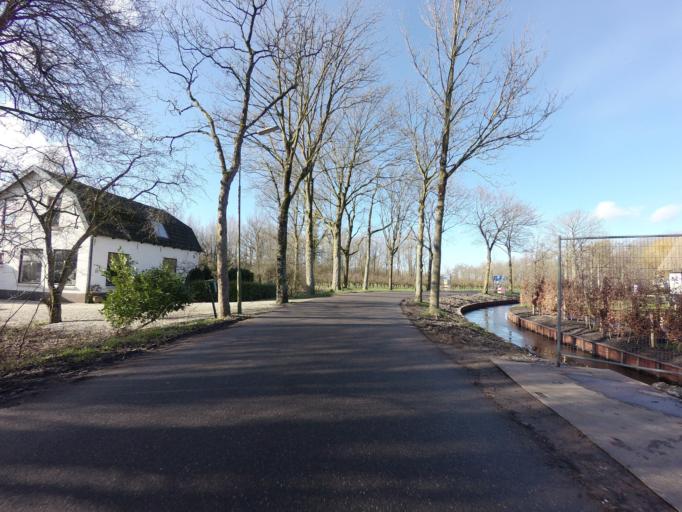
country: NL
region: Utrecht
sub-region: Gemeente Montfoort
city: Montfoort
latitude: 52.0987
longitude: 4.9607
